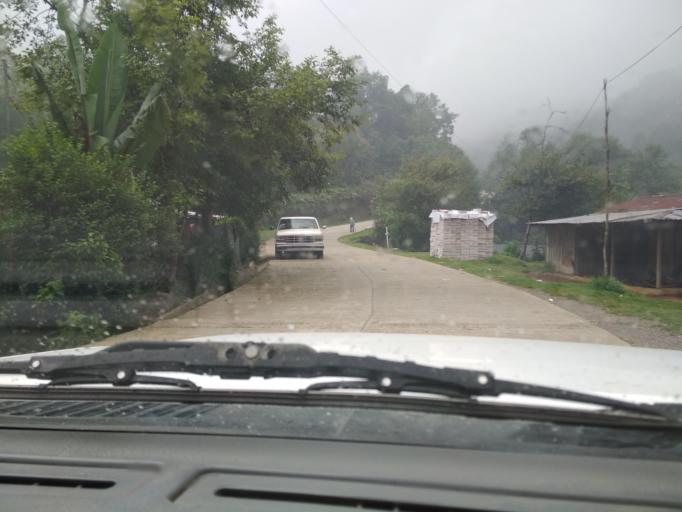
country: MX
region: Veracruz
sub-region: La Perla
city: Barrio de San Miguel
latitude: 18.9562
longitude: -97.1254
